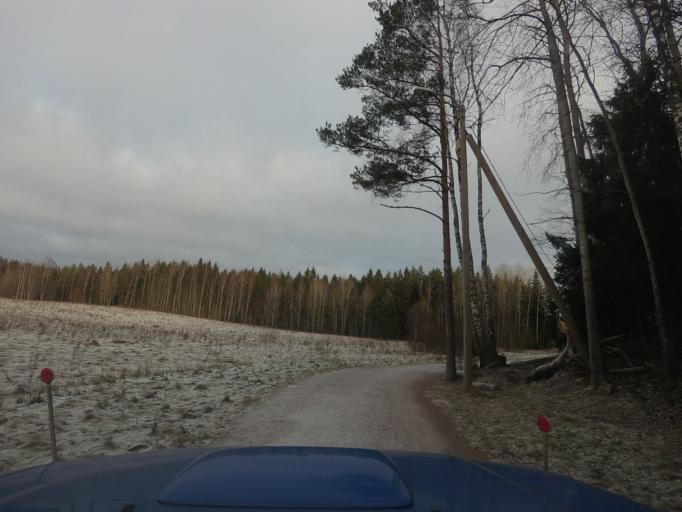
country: FI
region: Uusimaa
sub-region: Helsinki
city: Espoo
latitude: 60.1884
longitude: 24.6856
